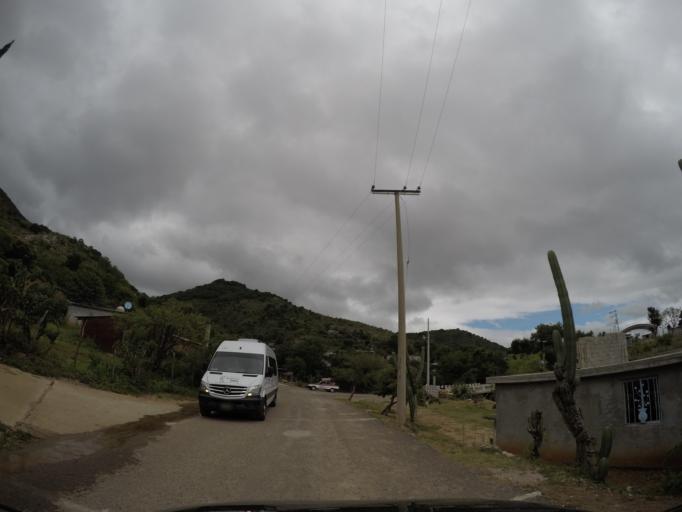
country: MX
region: Oaxaca
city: San Lorenzo Albarradas
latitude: 16.9021
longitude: -96.2610
